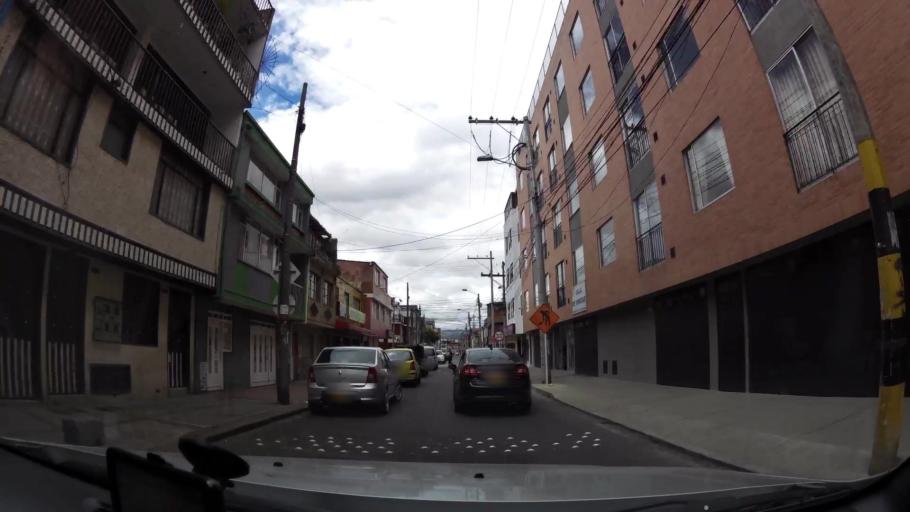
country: CO
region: Bogota D.C.
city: Bogota
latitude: 4.6026
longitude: -74.1054
